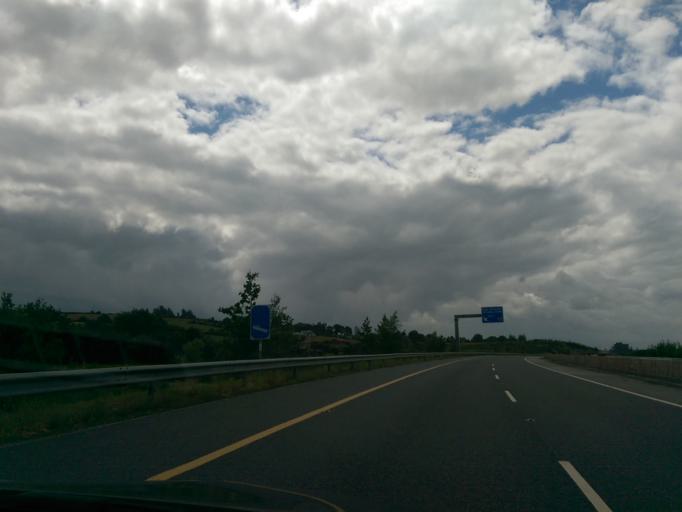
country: IE
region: Munster
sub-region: County Cork
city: Mitchelstown
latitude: 52.2427
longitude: -8.2714
